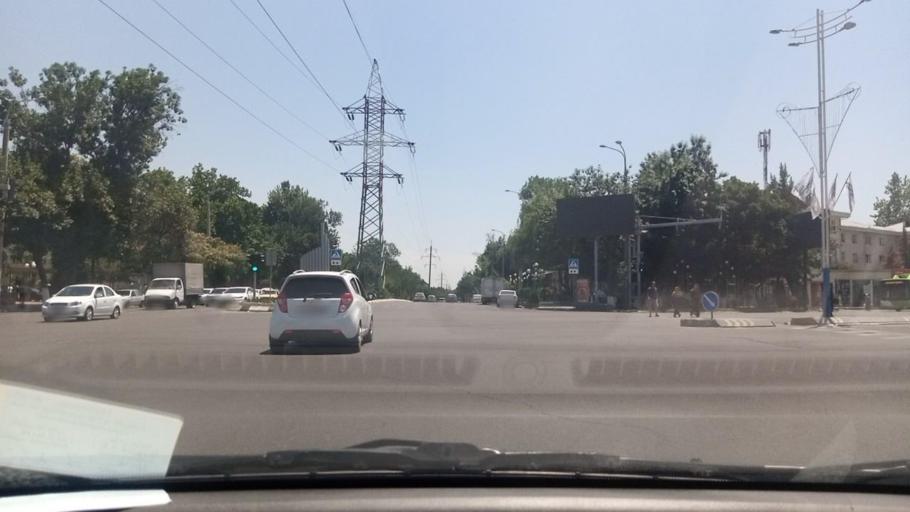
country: UZ
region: Toshkent Shahri
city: Tashkent
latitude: 41.2923
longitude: 69.1940
